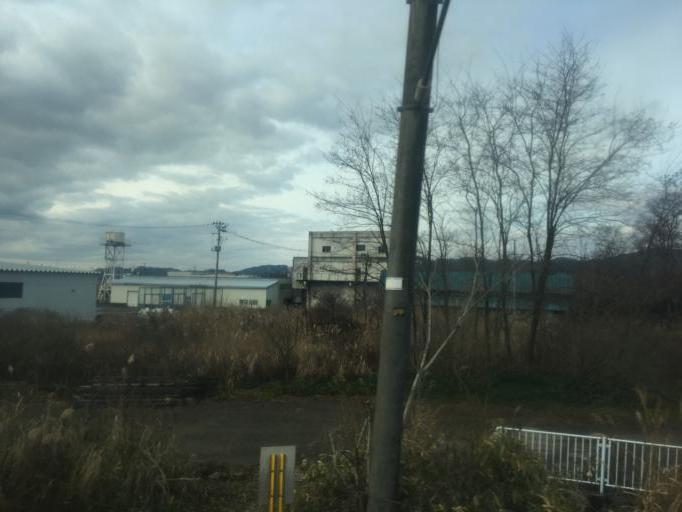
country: JP
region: Akita
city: Odate
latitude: 40.2954
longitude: 140.5662
